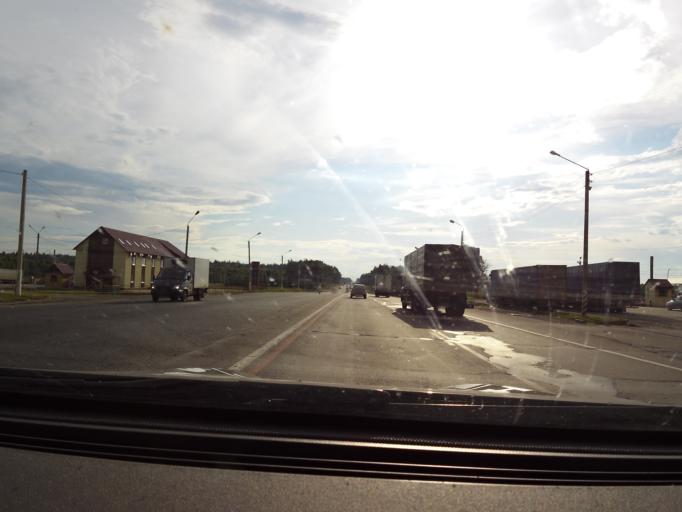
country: RU
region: Vladimir
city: Stepantsevo
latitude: 56.2305
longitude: 41.7361
